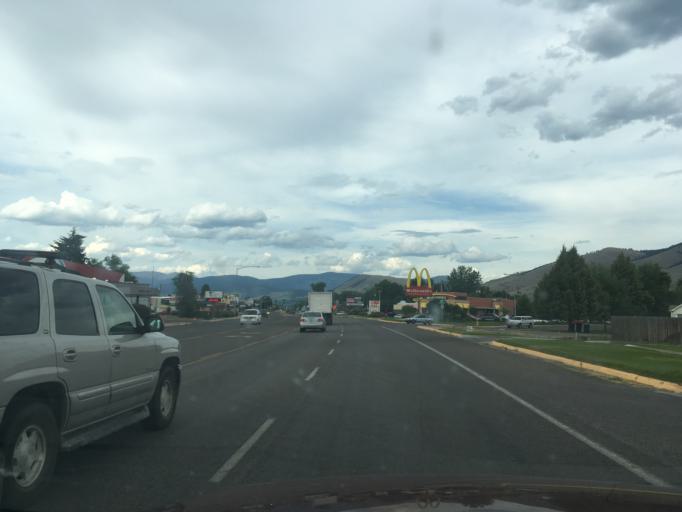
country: US
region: Montana
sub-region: Missoula County
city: Orchard Homes
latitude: 46.8394
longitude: -114.0315
